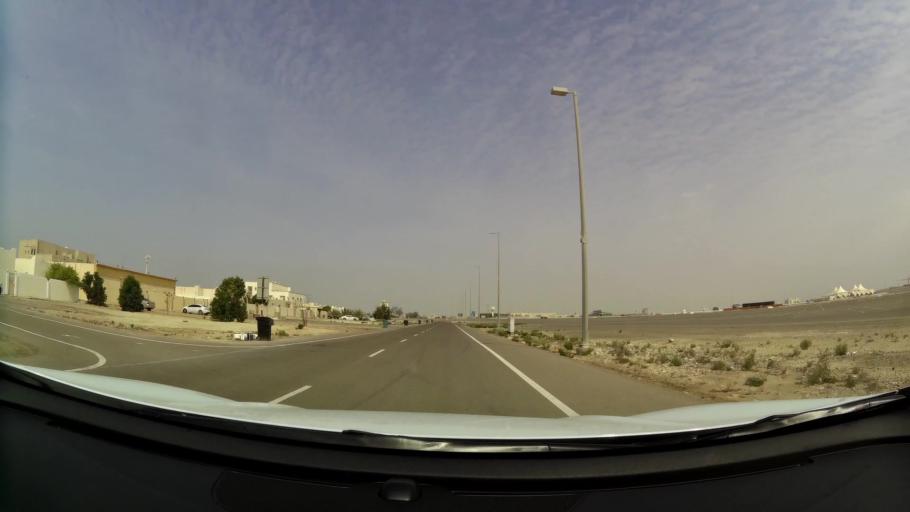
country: AE
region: Abu Dhabi
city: Abu Dhabi
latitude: 24.5353
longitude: 54.6722
